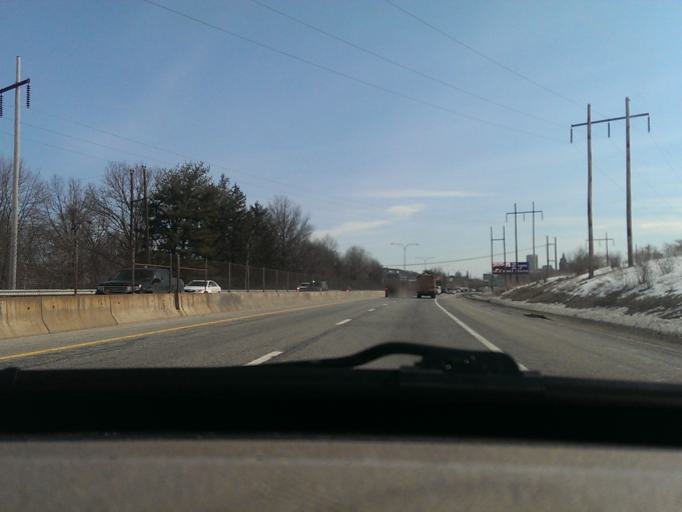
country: US
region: Rhode Island
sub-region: Providence County
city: Providence
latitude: 41.8468
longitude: -71.4218
